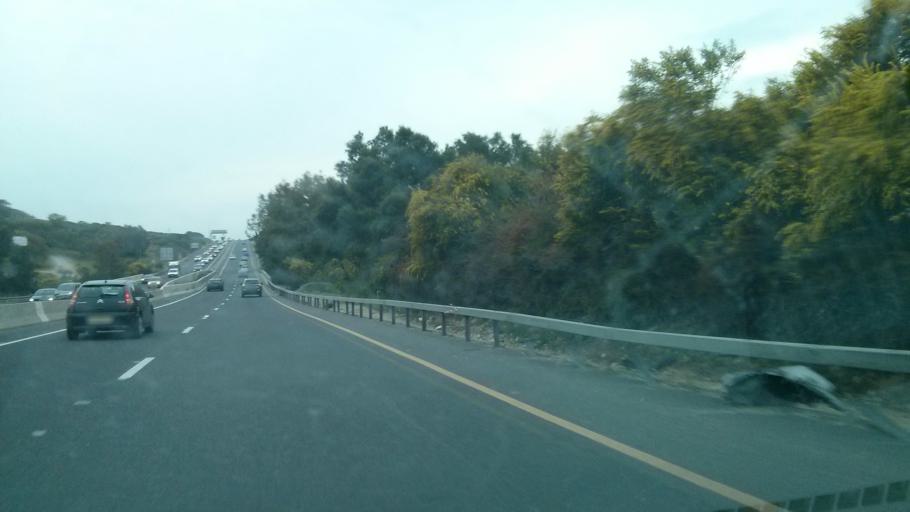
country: IL
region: Haifa
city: Hadera
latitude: 32.4679
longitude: 34.8974
